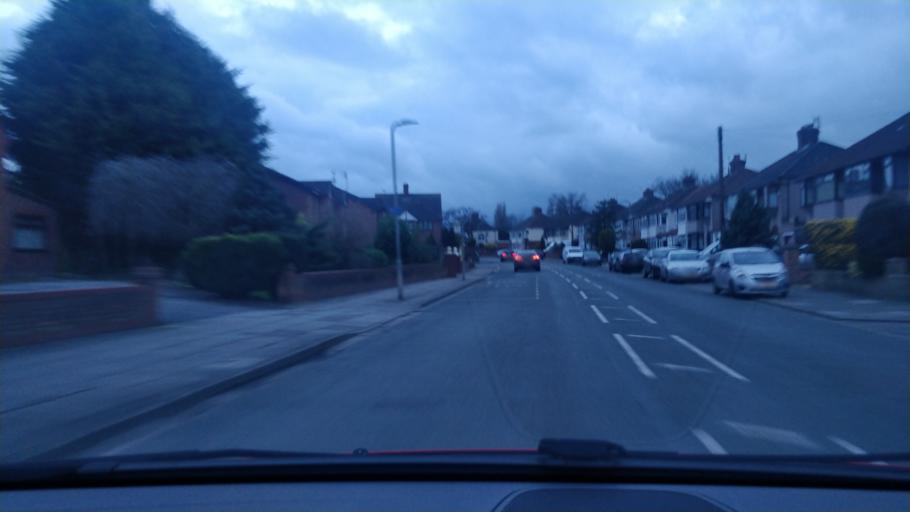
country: GB
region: England
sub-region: Knowsley
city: Knowsley
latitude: 53.4283
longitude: -2.8848
